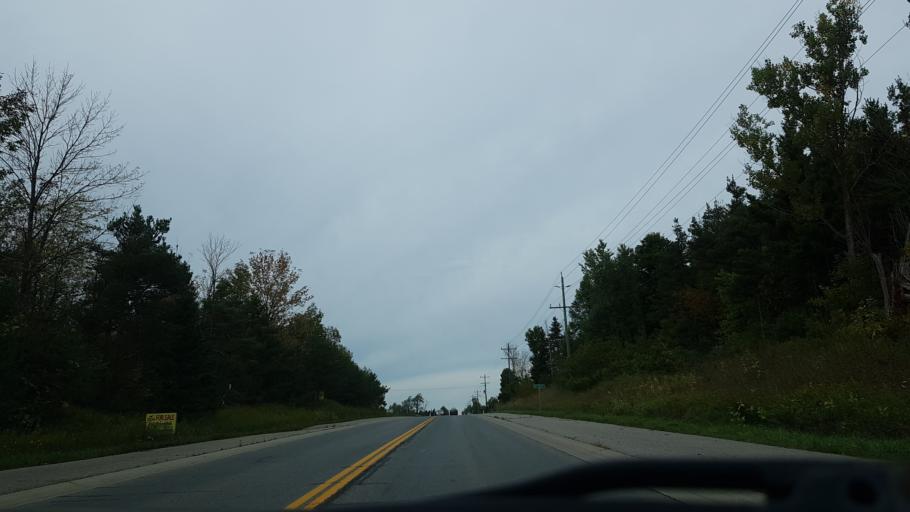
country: CA
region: Ontario
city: Orangeville
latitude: 43.9353
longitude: -79.9556
